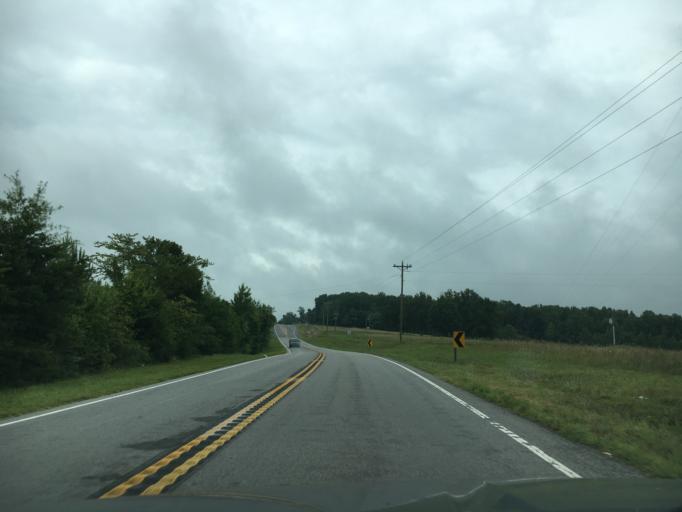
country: US
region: Virginia
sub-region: Halifax County
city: Mountain Road
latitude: 36.8563
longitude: -79.0054
